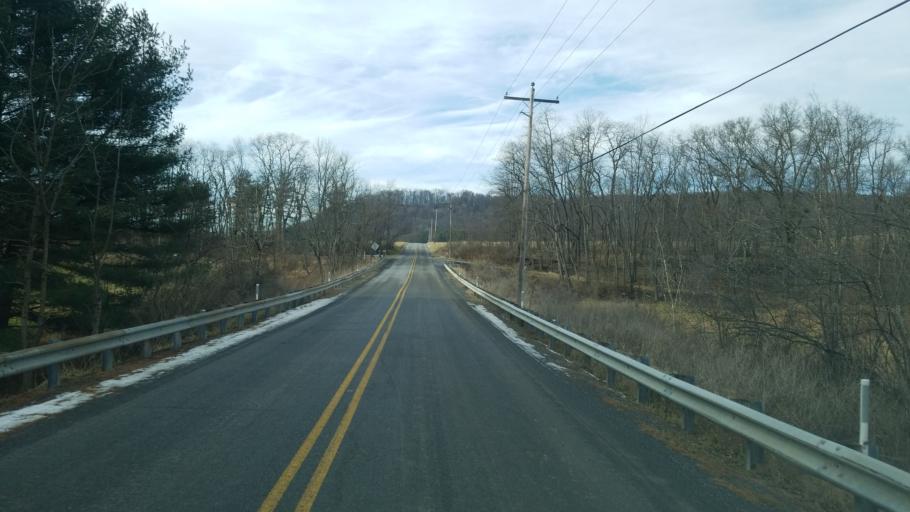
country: US
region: Pennsylvania
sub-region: Jefferson County
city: Punxsutawney
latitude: 40.8359
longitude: -79.1101
